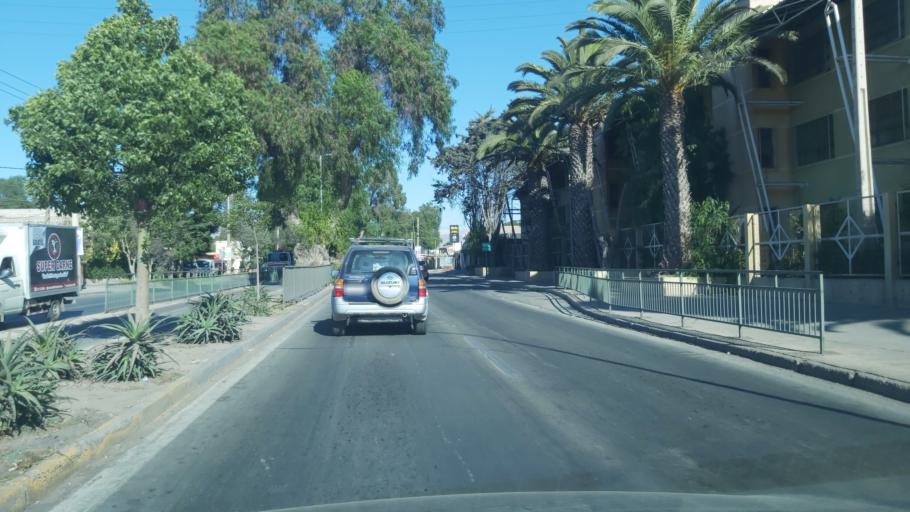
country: CL
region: Atacama
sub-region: Provincia de Copiapo
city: Copiapo
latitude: -27.3741
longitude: -70.3275
